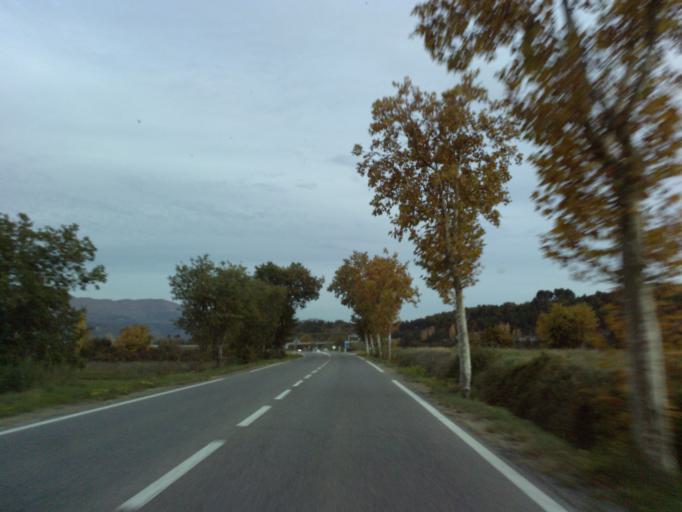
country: FR
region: Provence-Alpes-Cote d'Azur
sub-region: Departement des Alpes-de-Haute-Provence
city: Peipin
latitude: 44.1297
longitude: 5.9762
